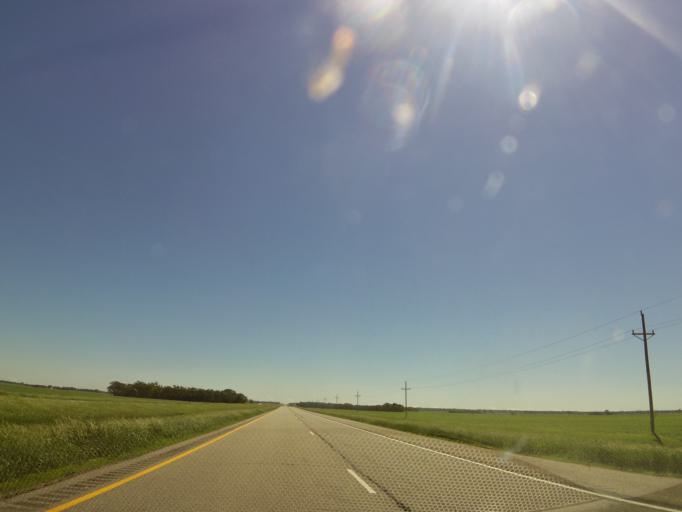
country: US
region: Minnesota
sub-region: Polk County
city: Crookston
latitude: 47.7604
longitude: -96.4803
